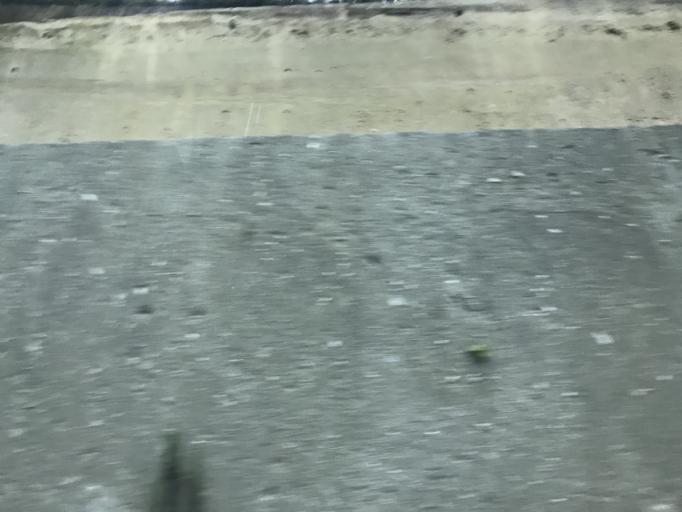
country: GT
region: Chimaltenango
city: El Tejar
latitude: 14.6377
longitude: -90.7891
